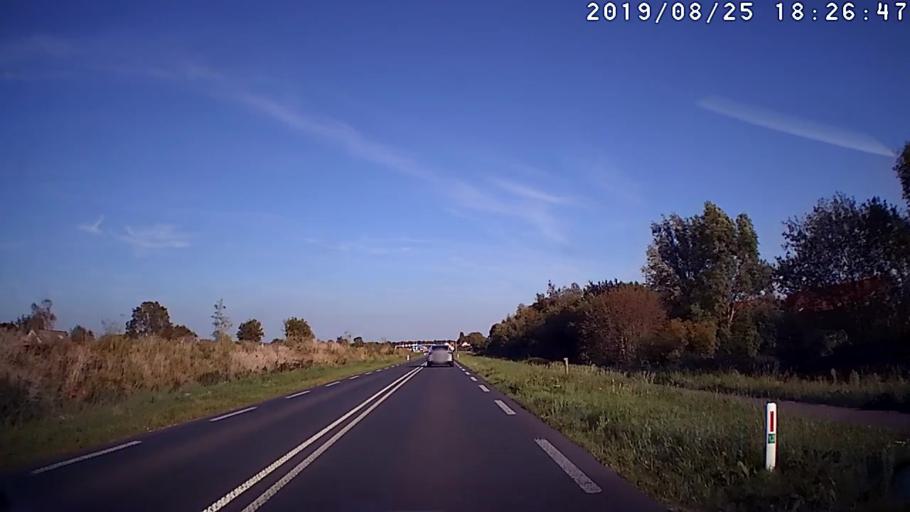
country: NL
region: Friesland
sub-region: Gemeente Lemsterland
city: Lemmer
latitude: 52.8501
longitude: 5.7056
